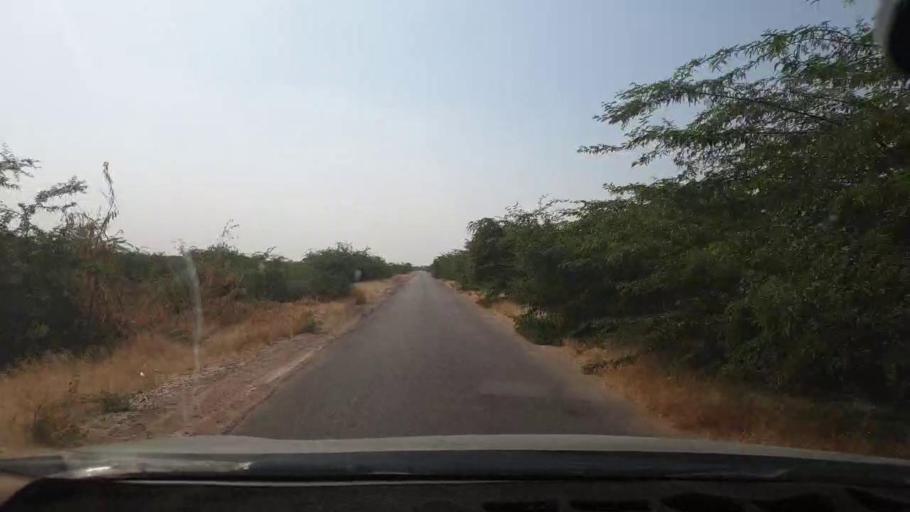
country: PK
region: Sindh
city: Malir Cantonment
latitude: 25.1053
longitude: 67.1992
